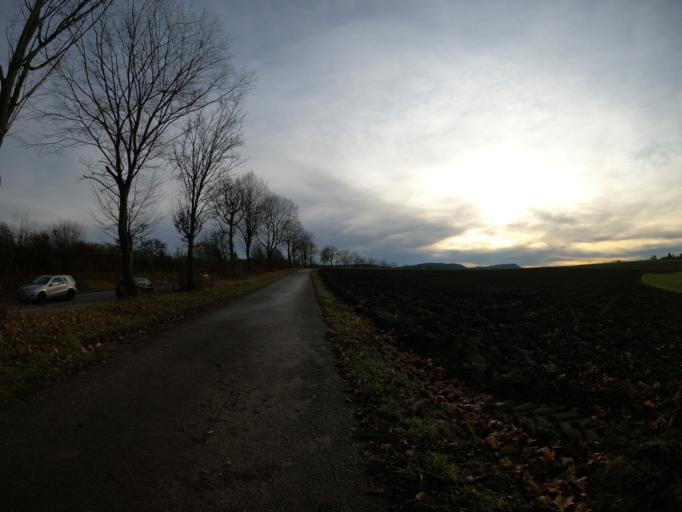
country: DE
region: Baden-Wuerttemberg
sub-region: Regierungsbezirk Stuttgart
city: Heiningen
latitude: 48.6810
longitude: 9.6633
